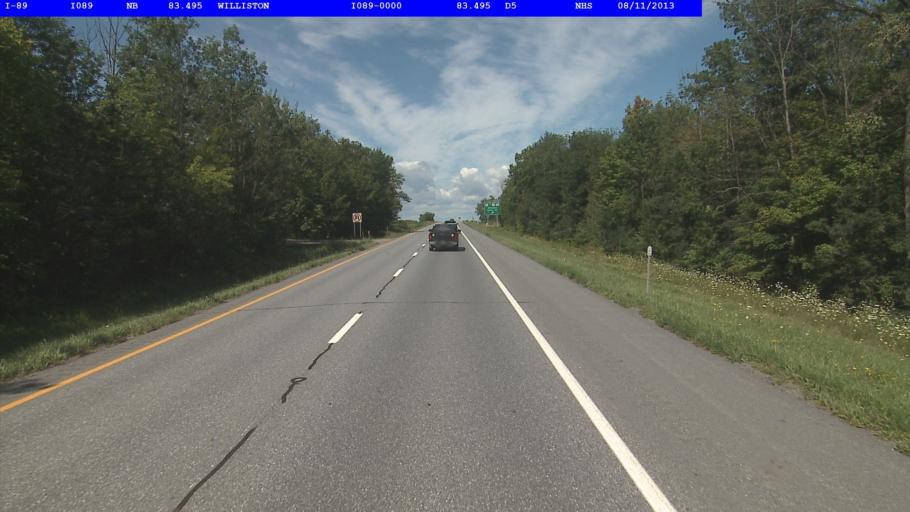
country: US
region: Vermont
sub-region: Chittenden County
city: Williston
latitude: 44.4386
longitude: -73.1056
